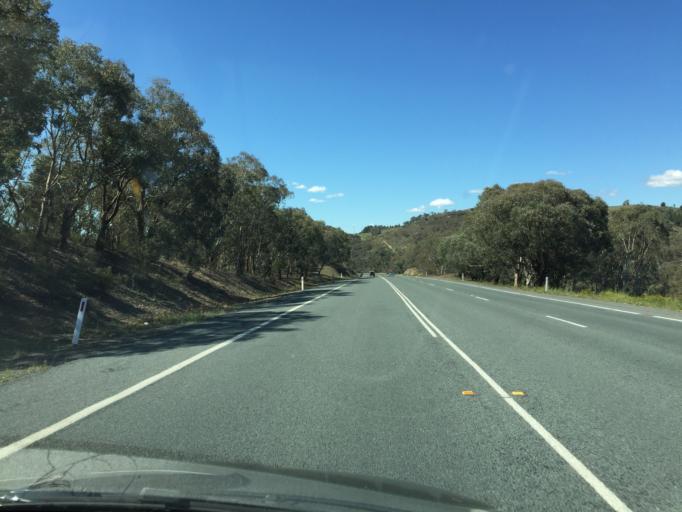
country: AU
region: Australian Capital Territory
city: Macarthur
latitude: -35.4497
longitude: 149.1299
